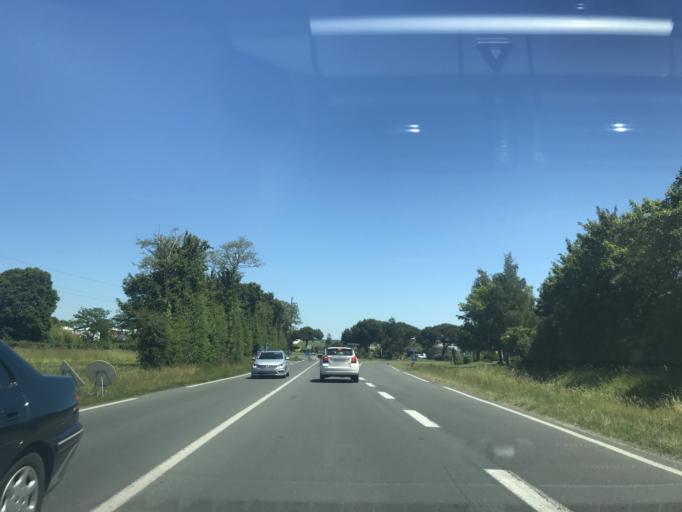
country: FR
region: Poitou-Charentes
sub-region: Departement de la Charente-Maritime
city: Royan
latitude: 45.6396
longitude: -1.0279
